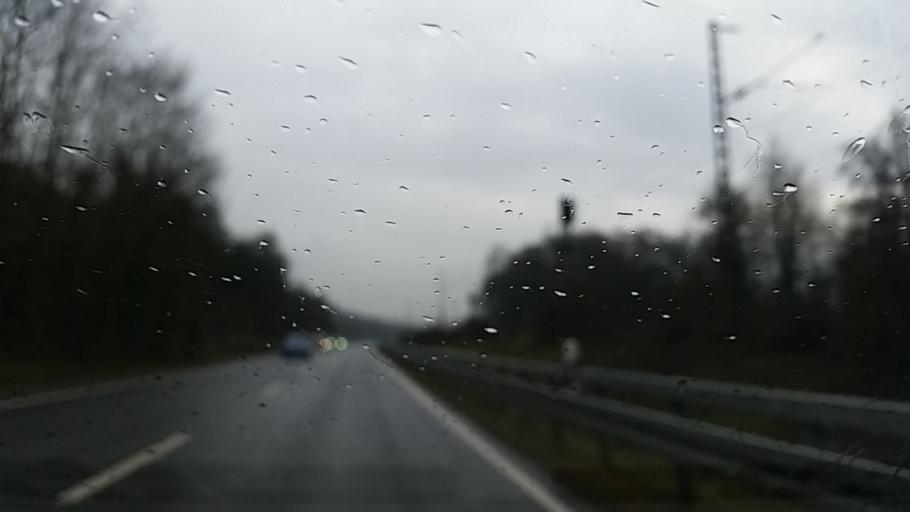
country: DE
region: Bavaria
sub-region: Regierungsbezirk Unterfranken
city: Karlstadt
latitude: 49.9899
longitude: 9.7602
